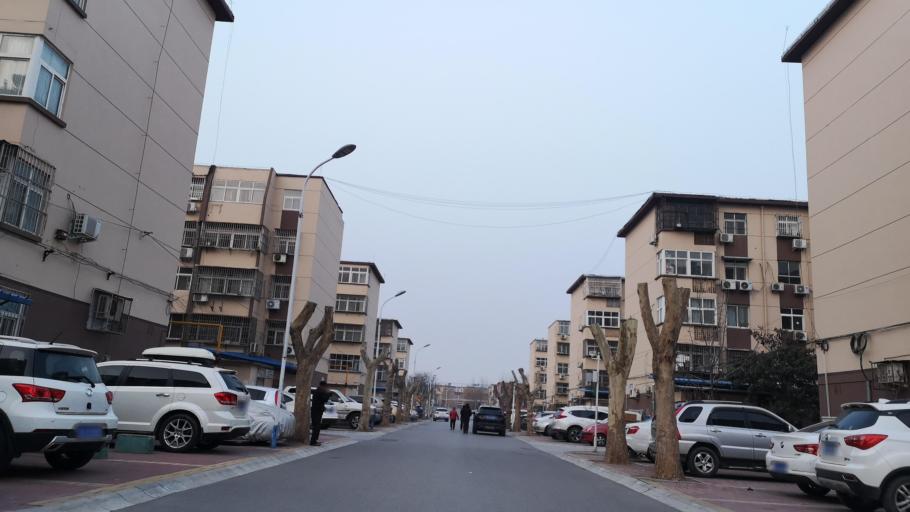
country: CN
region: Henan Sheng
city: Zhongyuanlu
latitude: 35.7831
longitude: 115.0744
